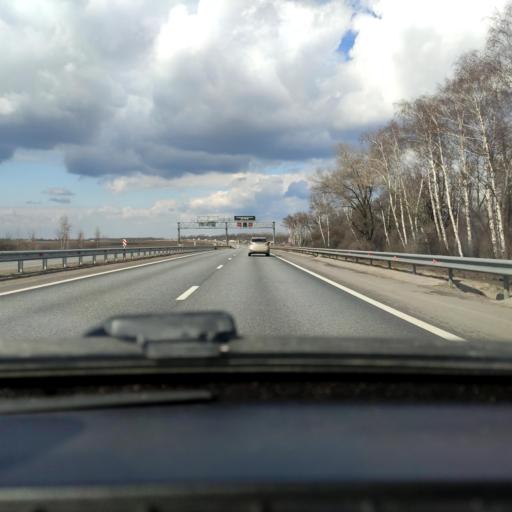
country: RU
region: Tula
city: Yefremov
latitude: 53.0214
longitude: 38.2134
